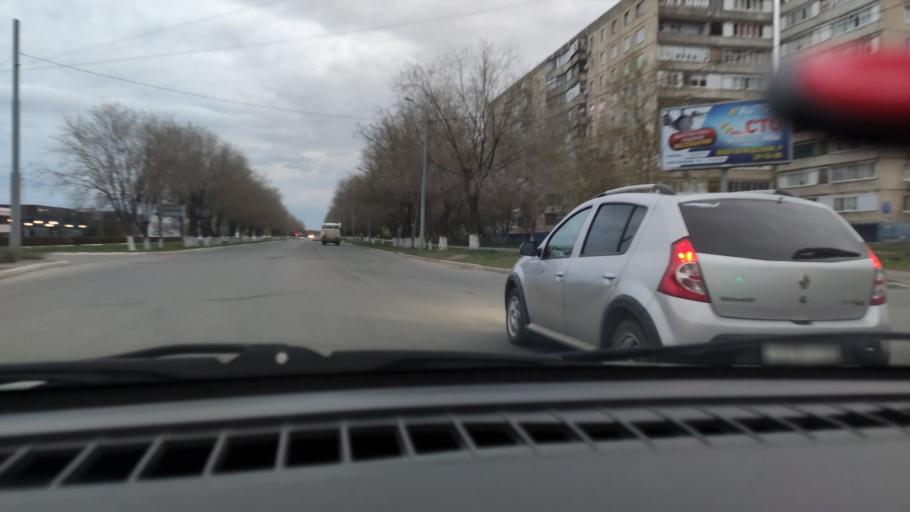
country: RU
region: Orenburg
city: Orenburg
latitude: 51.8451
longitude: 55.1331
